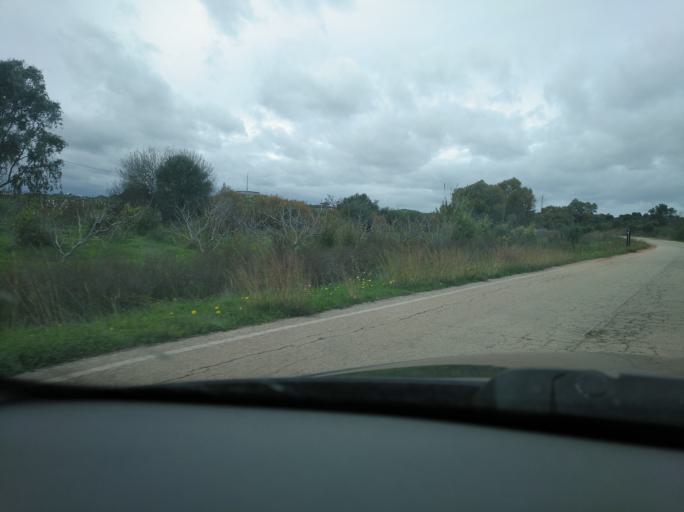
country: PT
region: Faro
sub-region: Vila Real de Santo Antonio
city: Monte Gordo
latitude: 37.1999
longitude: -7.4849
